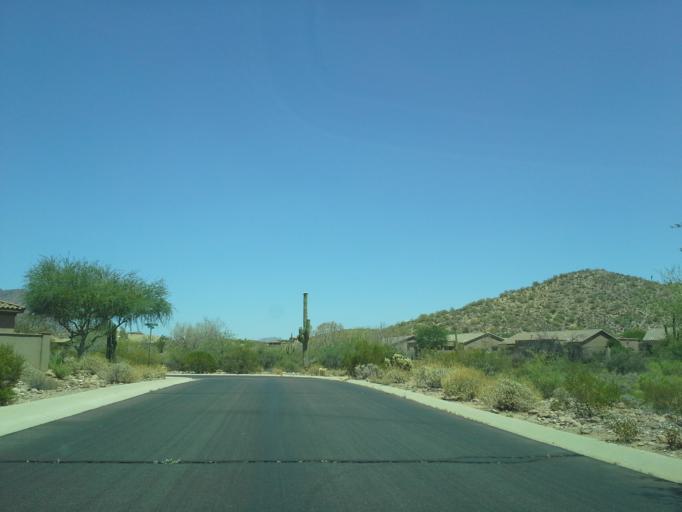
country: US
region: Arizona
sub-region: Pinal County
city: Apache Junction
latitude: 33.3809
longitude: -111.4585
